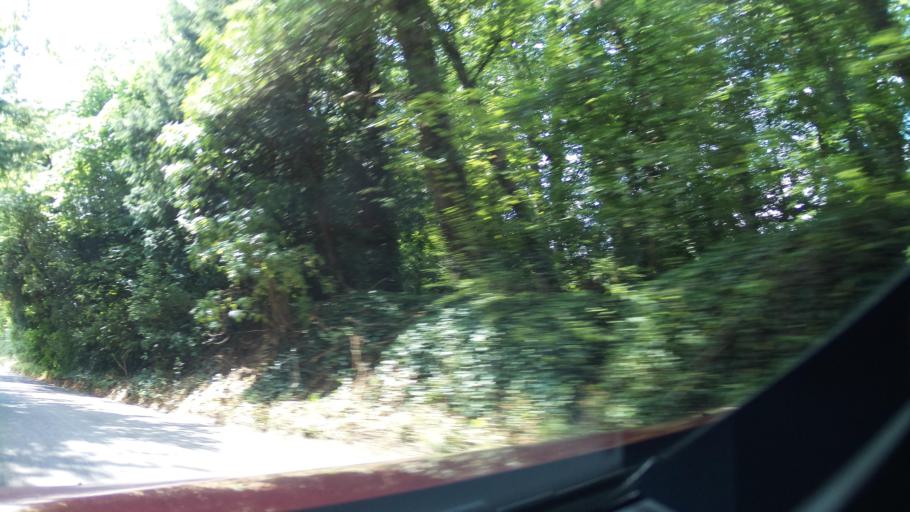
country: GB
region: England
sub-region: Wiltshire
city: Purton
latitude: 51.5845
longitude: -1.8637
